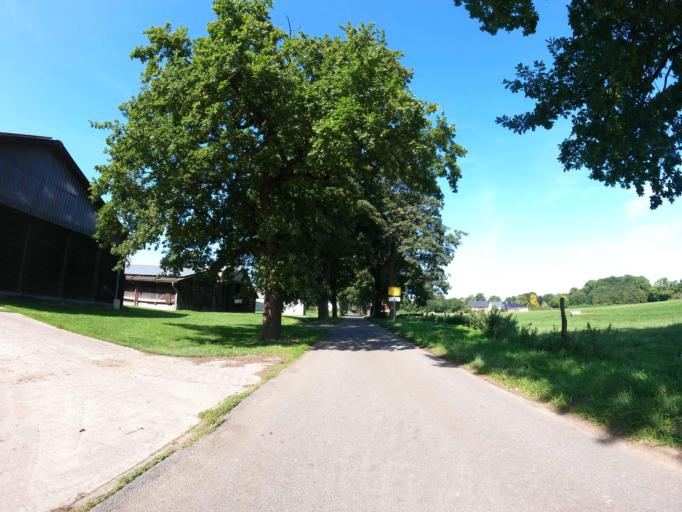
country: DE
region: Mecklenburg-Vorpommern
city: Prohn
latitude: 54.4021
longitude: 13.0182
